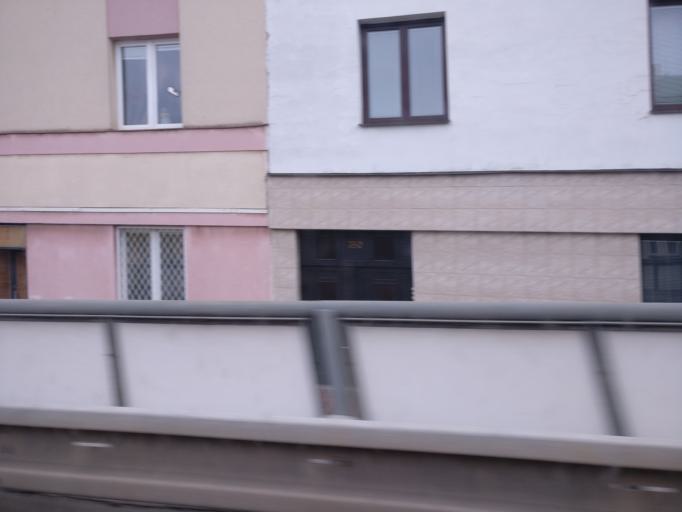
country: CZ
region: Pardubicky
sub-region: Okres Pardubice
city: Pardubice
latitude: 50.0333
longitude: 15.7891
